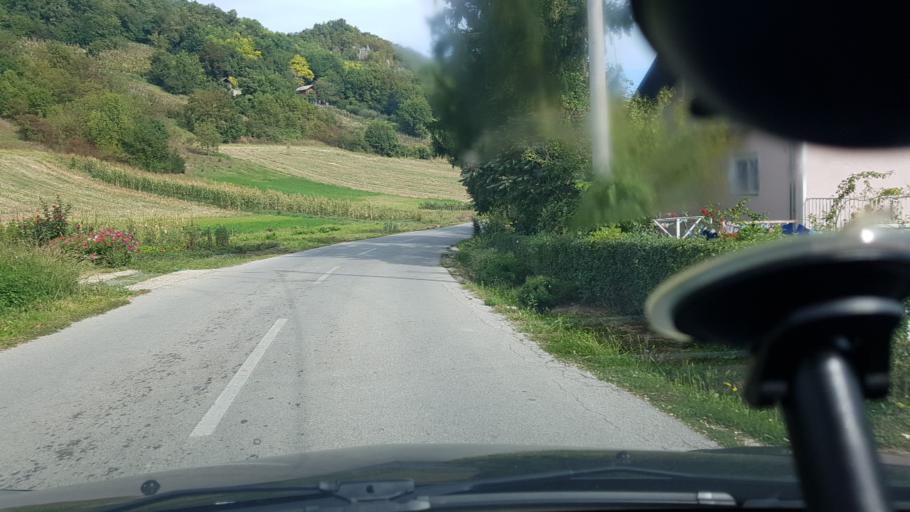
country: HR
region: Varazdinska
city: Ljubescica
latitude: 46.1013
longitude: 16.3494
